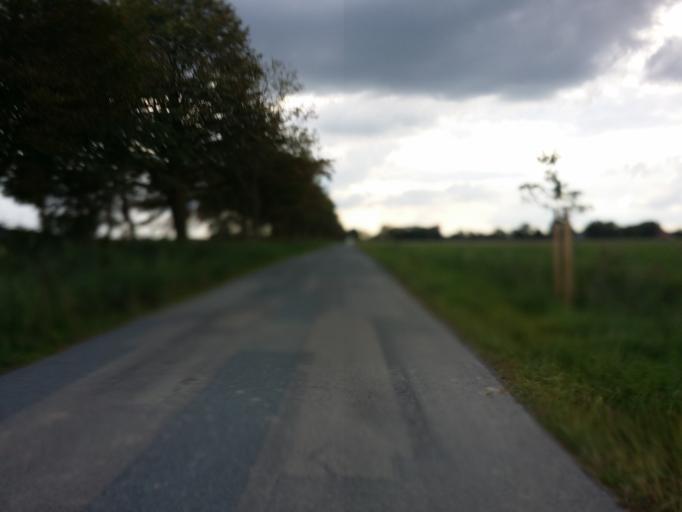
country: DE
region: Lower Saxony
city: Osten
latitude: 53.7321
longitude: 9.1932
